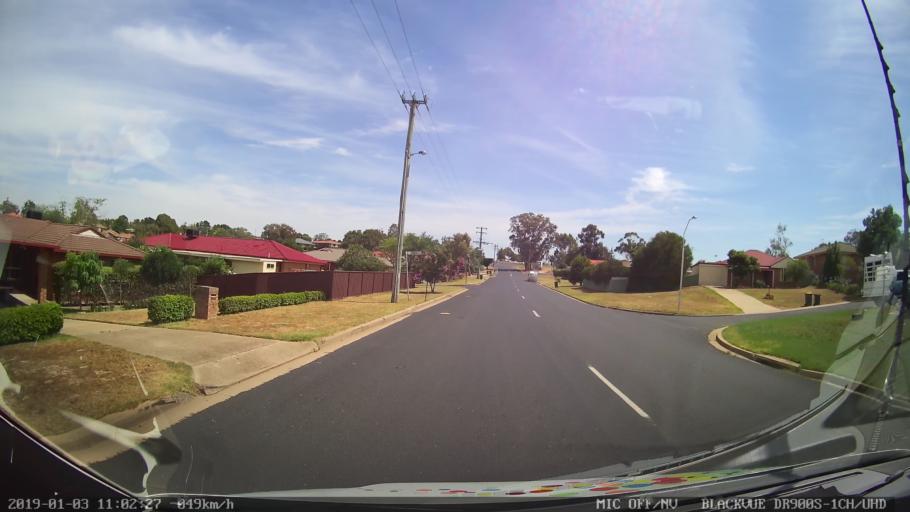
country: AU
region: New South Wales
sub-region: Young
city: Young
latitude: -34.2979
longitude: 148.2985
